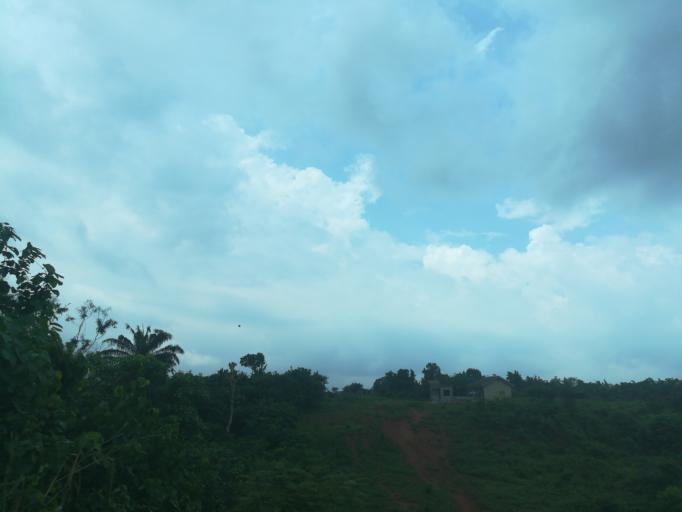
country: NG
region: Lagos
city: Ikorodu
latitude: 6.6634
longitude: 3.6269
